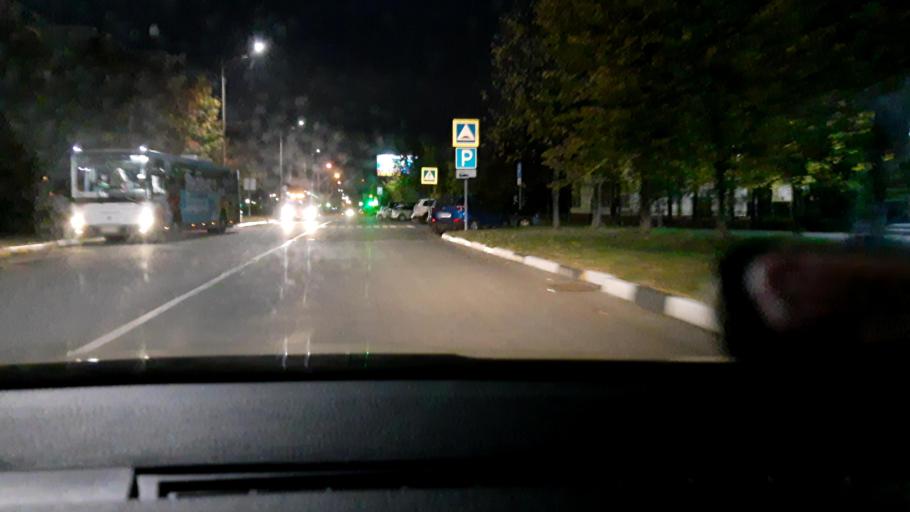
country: RU
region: Moskovskaya
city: Krasnoznamensk
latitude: 55.5984
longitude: 37.0355
